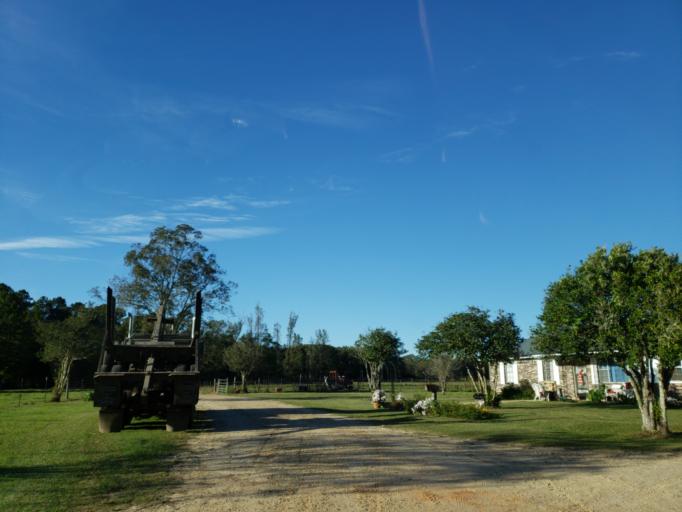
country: US
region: Mississippi
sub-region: Perry County
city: Richton
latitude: 31.3673
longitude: -88.8115
